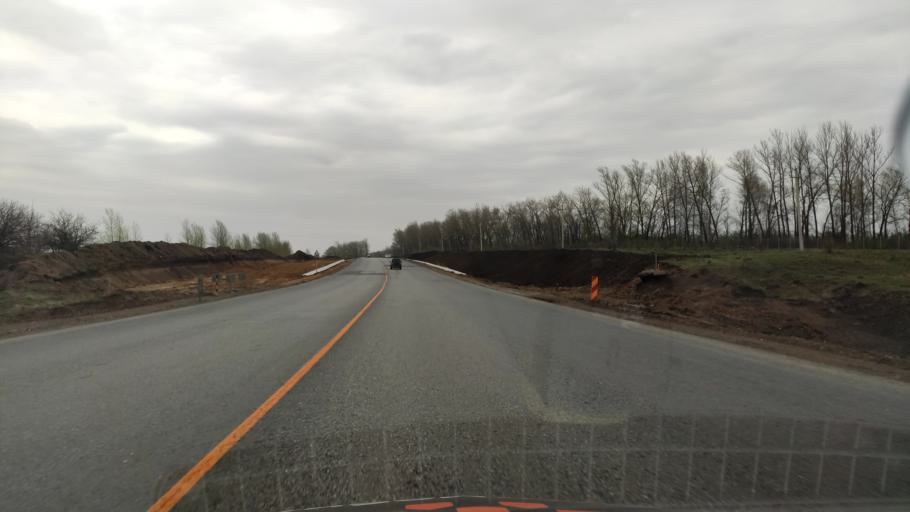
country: RU
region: Kursk
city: Gorshechnoye
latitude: 51.5490
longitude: 38.0501
